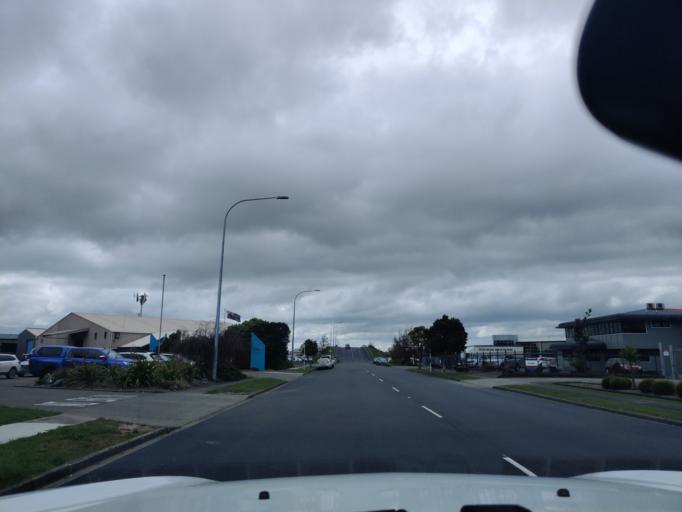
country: NZ
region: Manawatu-Wanganui
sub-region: Palmerston North City
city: Palmerston North
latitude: -40.3397
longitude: 175.6433
